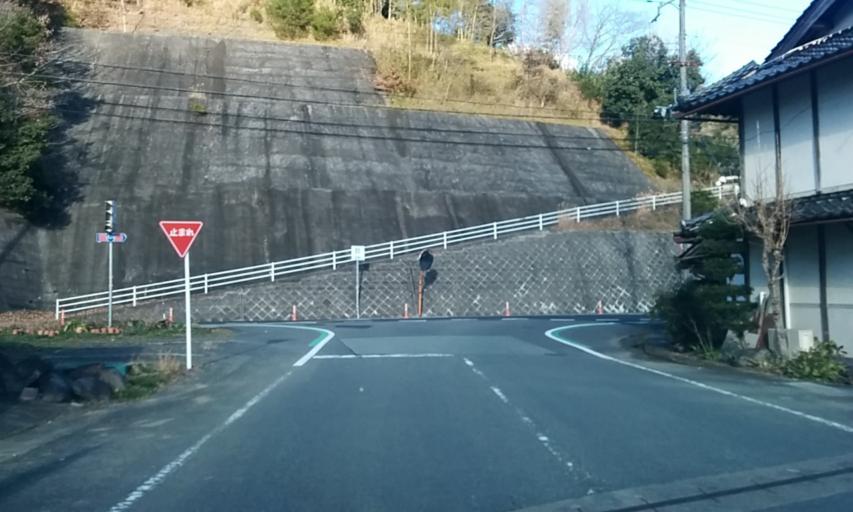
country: JP
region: Kyoto
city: Fukuchiyama
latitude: 35.2825
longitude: 135.0354
